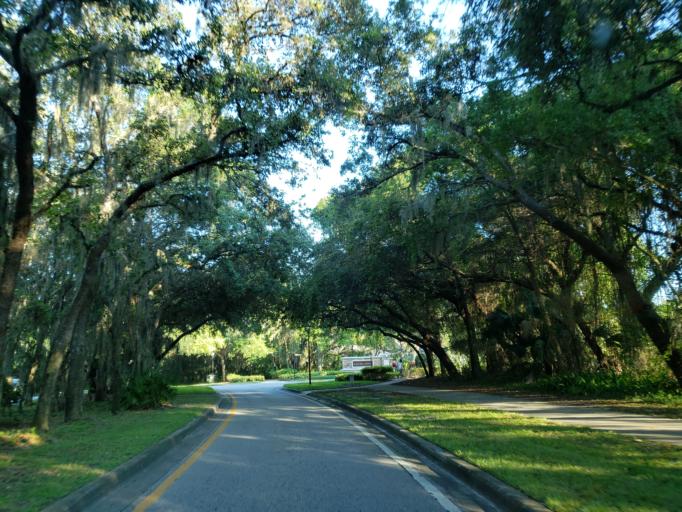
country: US
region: Florida
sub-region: Hillsborough County
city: Boyette
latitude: 27.8387
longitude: -82.2352
